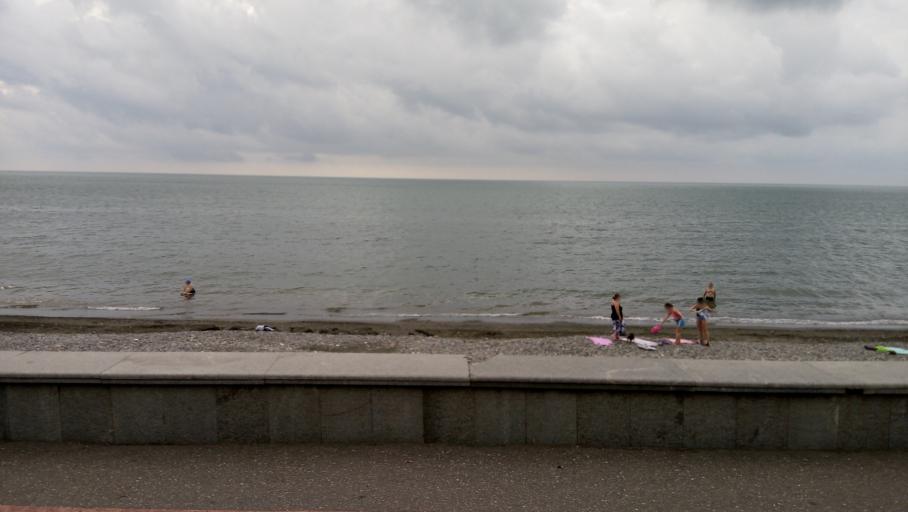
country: GE
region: Ajaria
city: Makhinjauri
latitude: 41.6591
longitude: 41.6767
